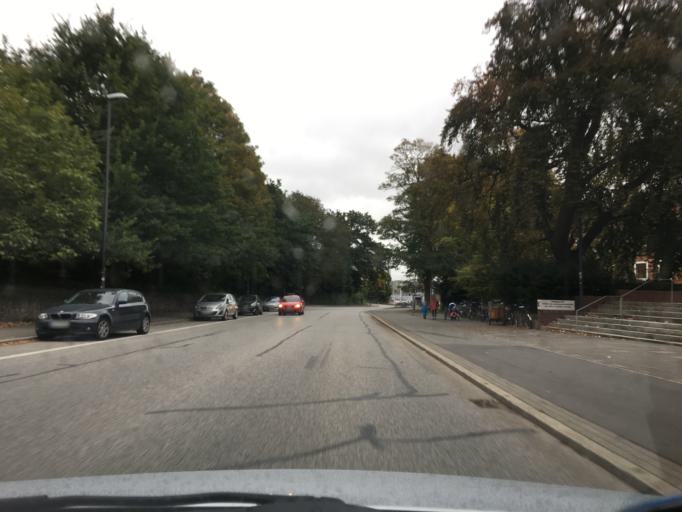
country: DE
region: Schleswig-Holstein
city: Kiel
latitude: 54.3369
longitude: 10.1535
